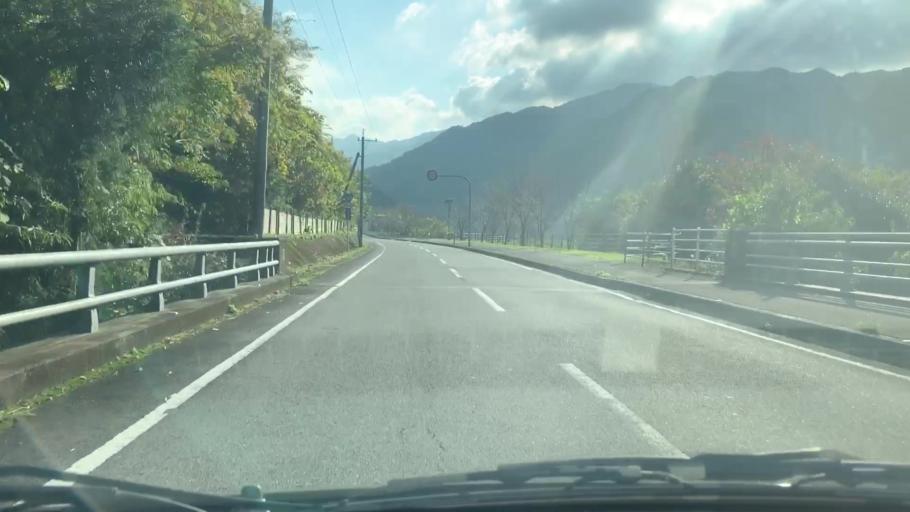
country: JP
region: Saga Prefecture
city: Kashima
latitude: 33.0371
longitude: 130.0707
